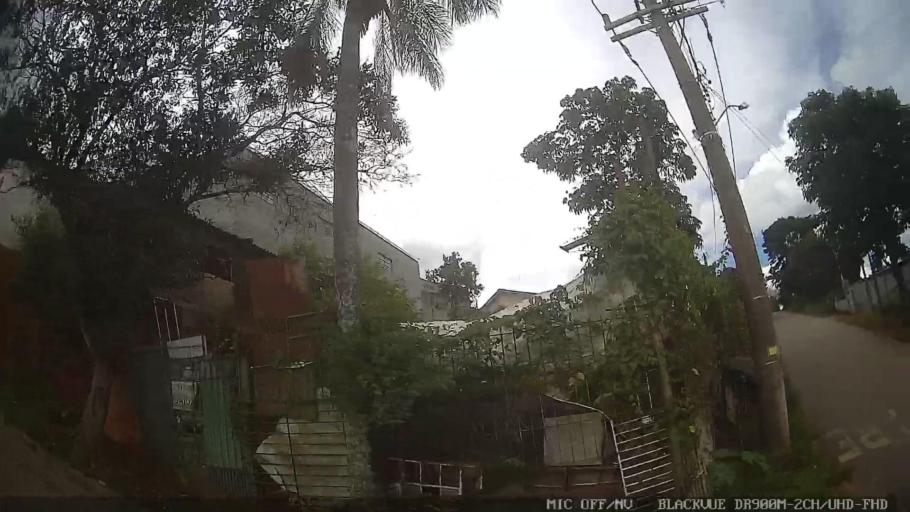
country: BR
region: Minas Gerais
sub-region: Extrema
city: Extrema
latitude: -22.7460
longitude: -46.3732
